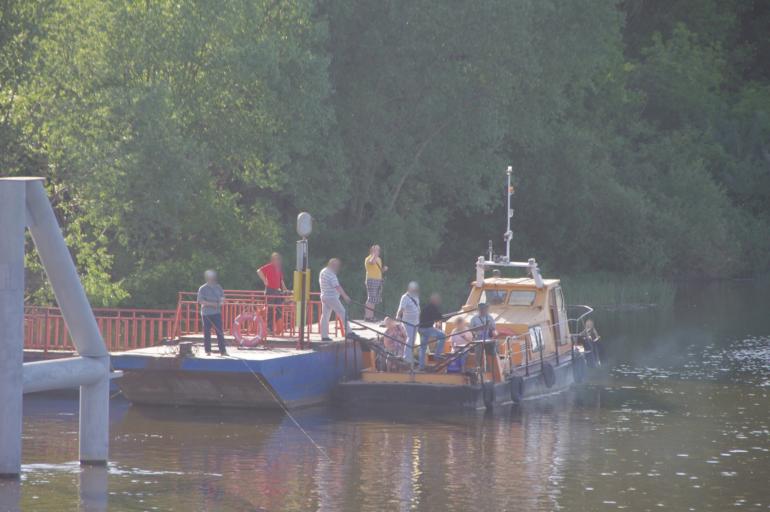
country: RU
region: Moskovskaya
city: Kolomna
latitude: 55.0958
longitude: 38.8003
